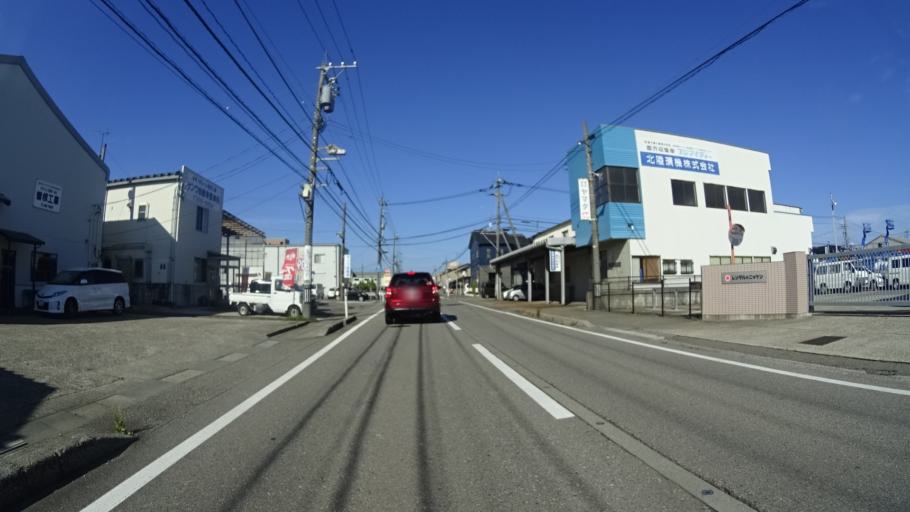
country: JP
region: Ishikawa
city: Kanazawa-shi
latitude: 36.6026
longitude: 136.6073
